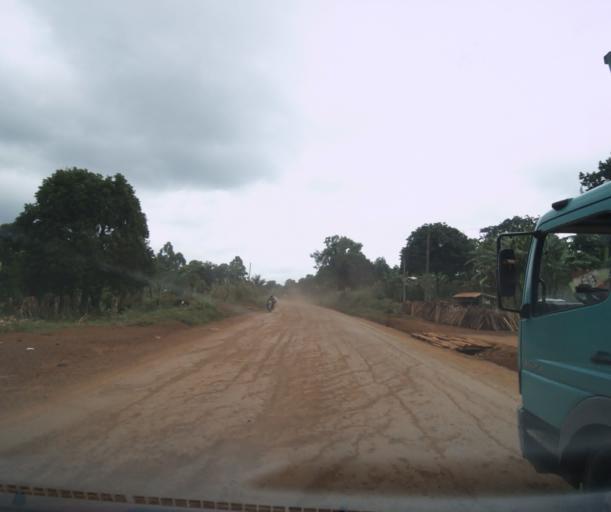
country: CM
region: West
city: Mbouda
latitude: 5.6681
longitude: 10.2187
